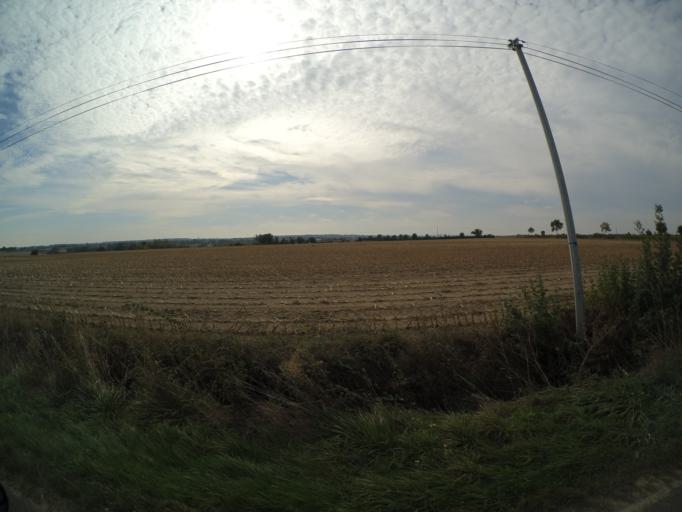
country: FR
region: Pays de la Loire
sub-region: Departement de Maine-et-Loire
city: Thouarce
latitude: 47.2091
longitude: -0.5078
